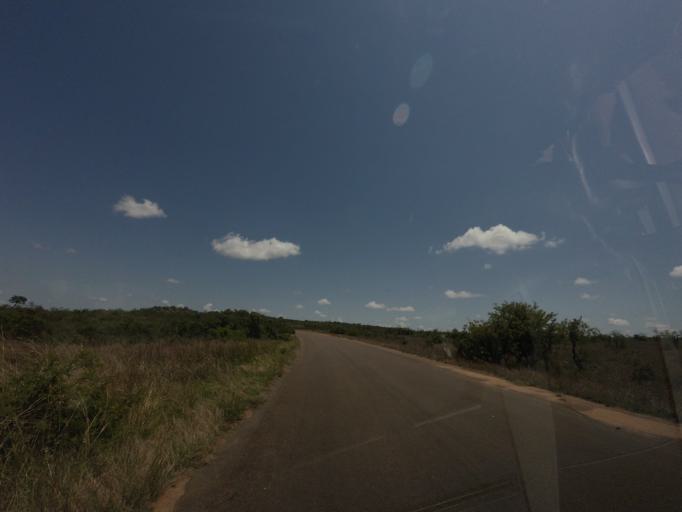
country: ZA
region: Mpumalanga
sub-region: Ehlanzeni District
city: Komatipoort
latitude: -24.8721
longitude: 31.9005
